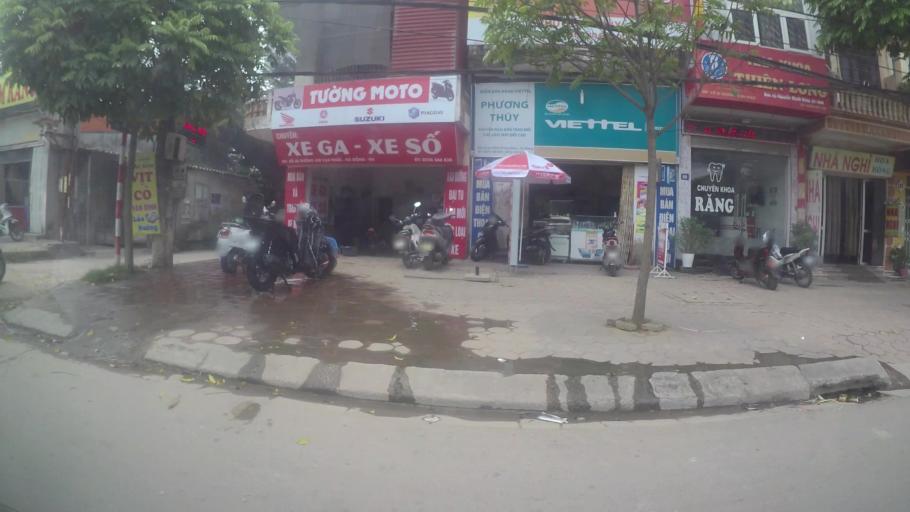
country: VN
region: Ha Noi
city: Ha Dong
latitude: 20.9793
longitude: 105.7725
